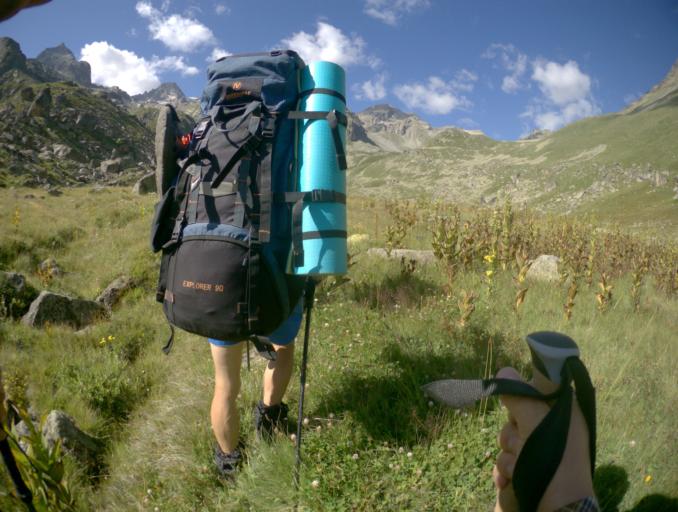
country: RU
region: Karachayevo-Cherkesiya
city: Uchkulan
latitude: 43.3331
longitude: 42.1152
